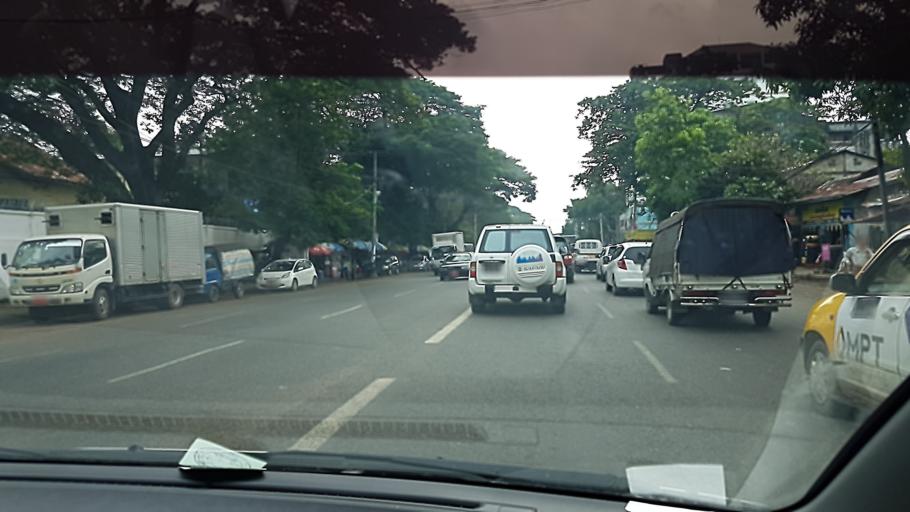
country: MM
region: Yangon
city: Yangon
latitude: 16.7916
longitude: 96.1275
